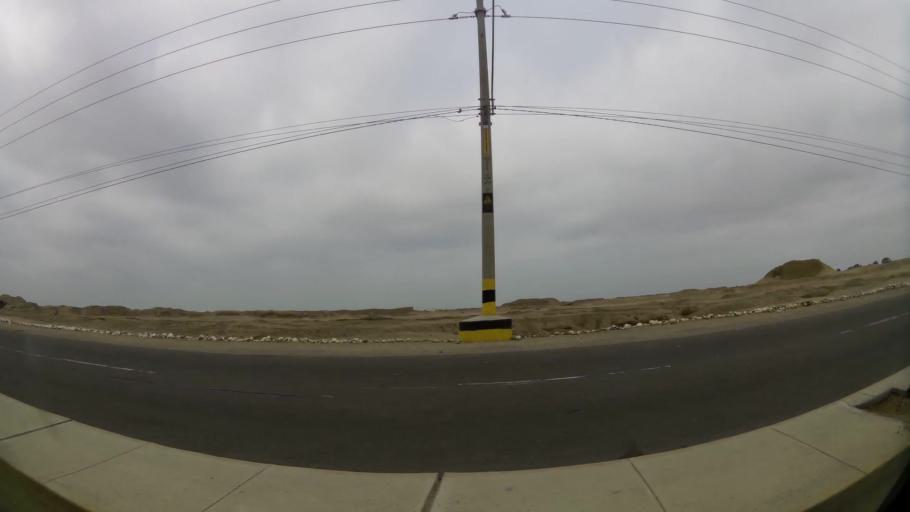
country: PE
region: La Libertad
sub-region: Provincia de Trujillo
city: La Esperanza
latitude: -8.0980
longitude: -79.0688
